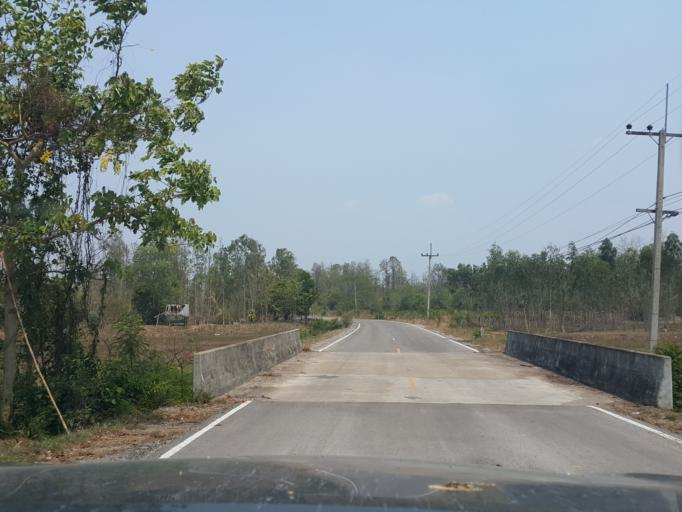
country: TH
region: Lampang
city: Mae Phrik
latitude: 17.5643
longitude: 99.0934
